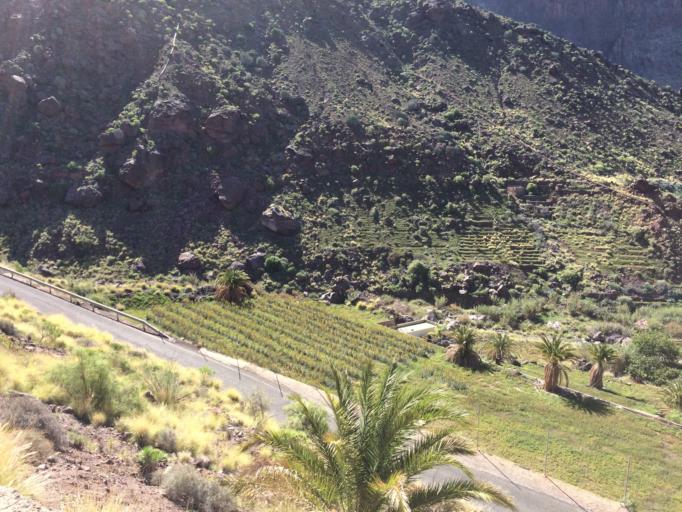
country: ES
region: Canary Islands
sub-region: Provincia de Las Palmas
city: San Nicolas
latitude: 27.9857
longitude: -15.7612
